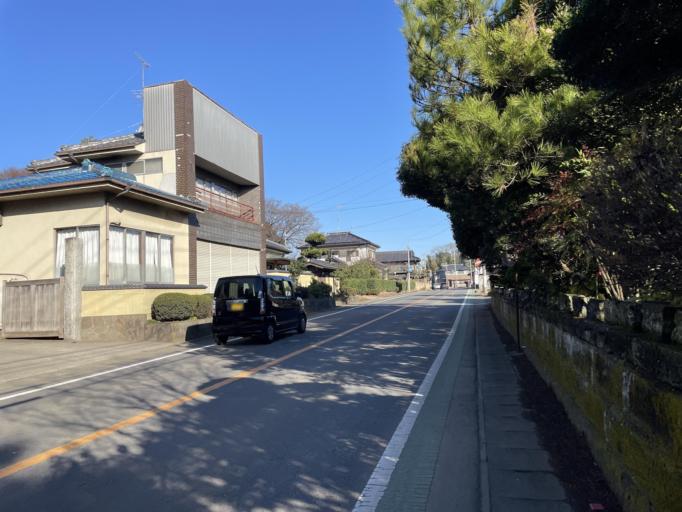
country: JP
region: Tochigi
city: Oyama
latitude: 36.2099
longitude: 139.8227
